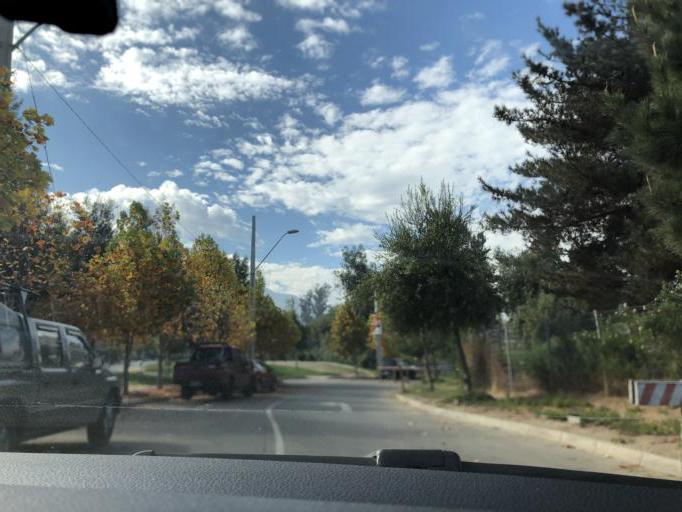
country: CL
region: Santiago Metropolitan
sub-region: Provincia de Cordillera
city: Puente Alto
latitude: -33.5782
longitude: -70.5427
